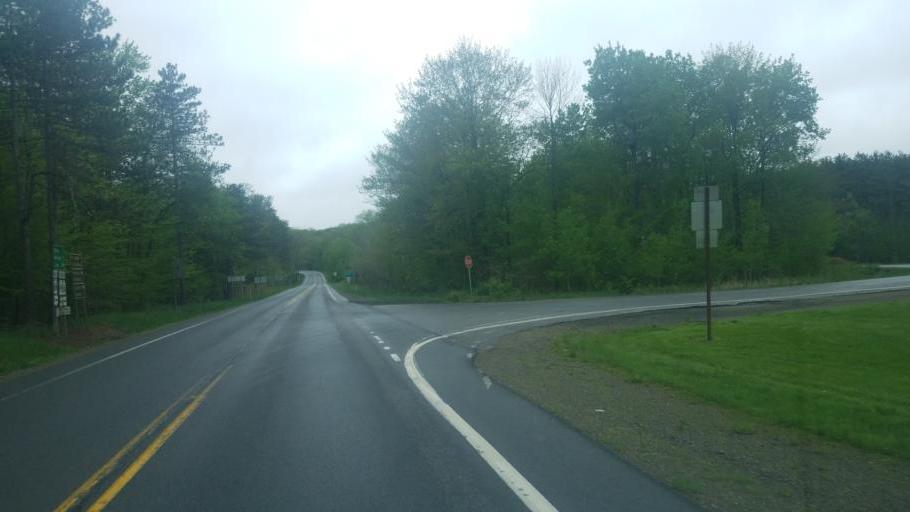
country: US
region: Pennsylvania
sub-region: McKean County
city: Kane
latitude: 41.5800
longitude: -78.9332
